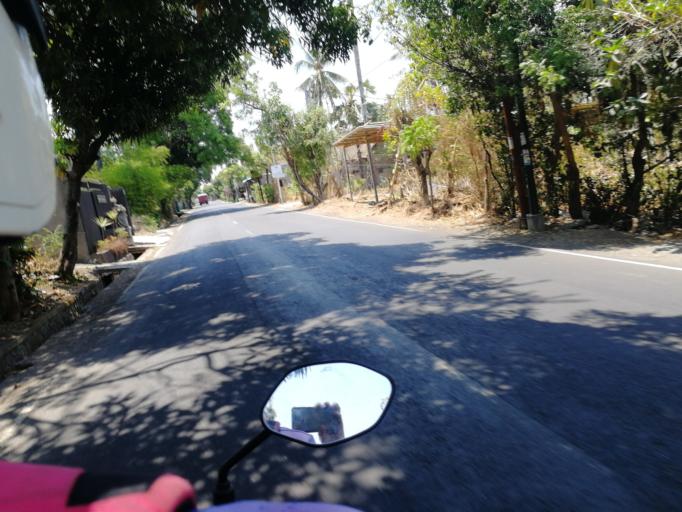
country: ID
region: Bali
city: Banjar Trunyan
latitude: -8.1435
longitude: 115.3954
